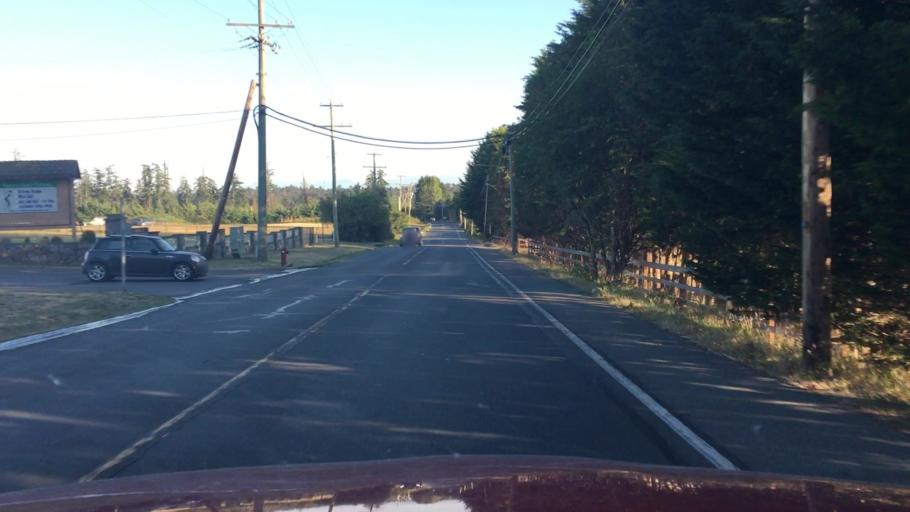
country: CA
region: British Columbia
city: Victoria
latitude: 48.4832
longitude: -123.3546
